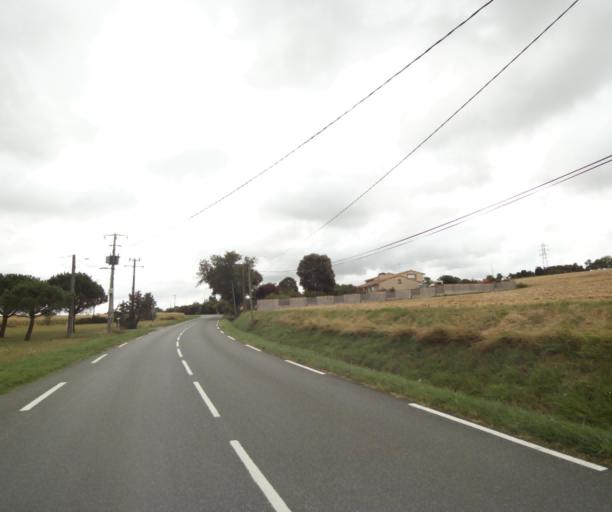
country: FR
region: Midi-Pyrenees
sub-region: Departement de la Haute-Garonne
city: Flourens
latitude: 43.5991
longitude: 1.5309
